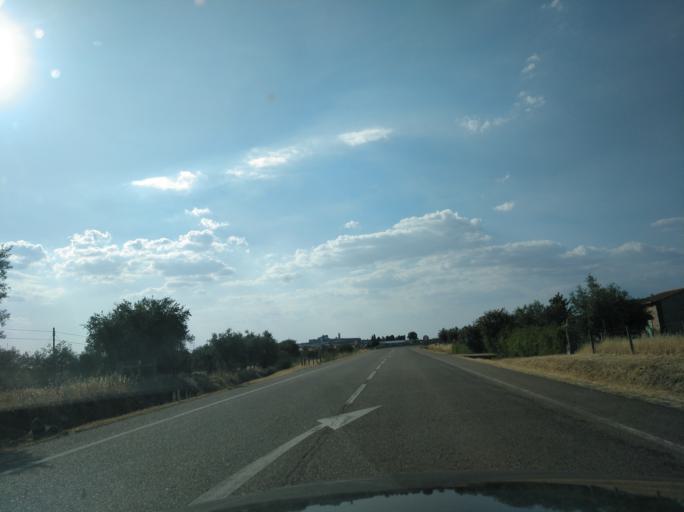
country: PT
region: Evora
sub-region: Mourao
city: Mourao
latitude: 38.3779
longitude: -7.3294
